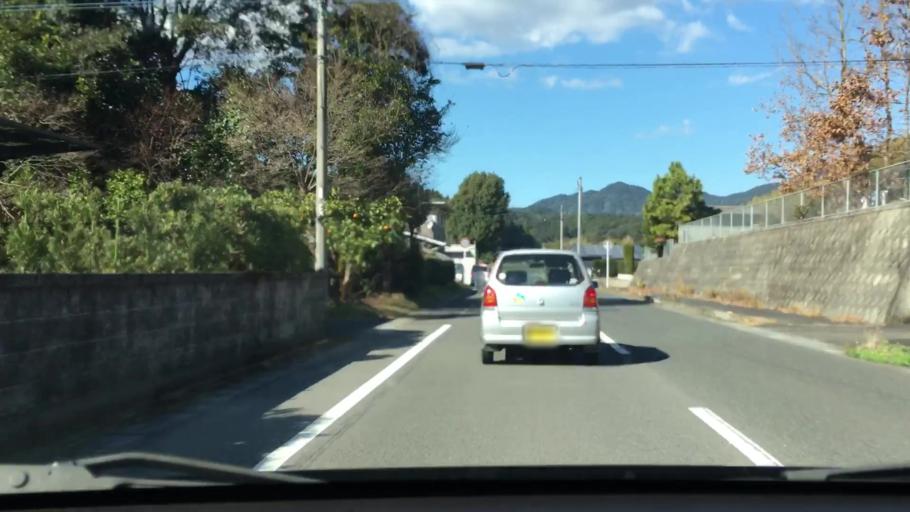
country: JP
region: Kagoshima
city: Ijuin
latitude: 31.6918
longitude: 130.4640
